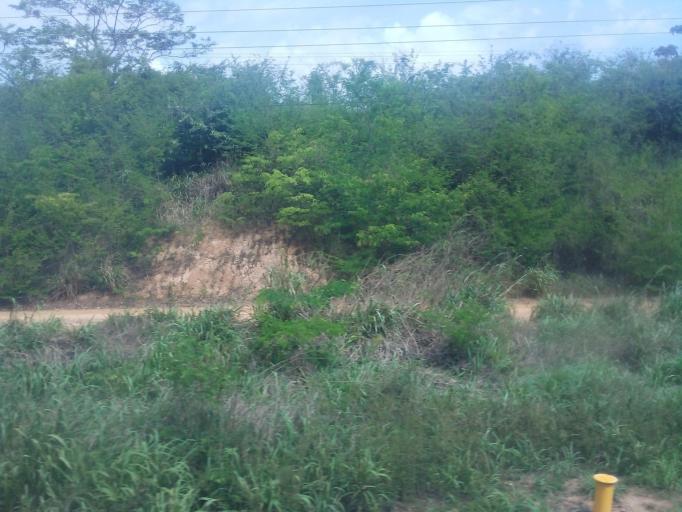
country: BR
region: Maranhao
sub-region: Santa Ines
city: Santa Ines
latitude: -3.8742
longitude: -46.1970
